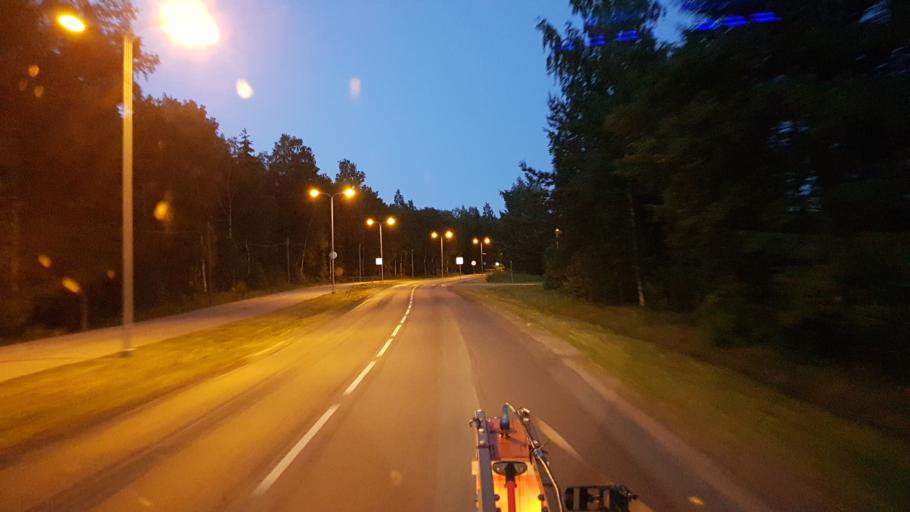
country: EE
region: Harju
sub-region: Harku vald
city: Tabasalu
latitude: 59.4354
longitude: 24.6143
